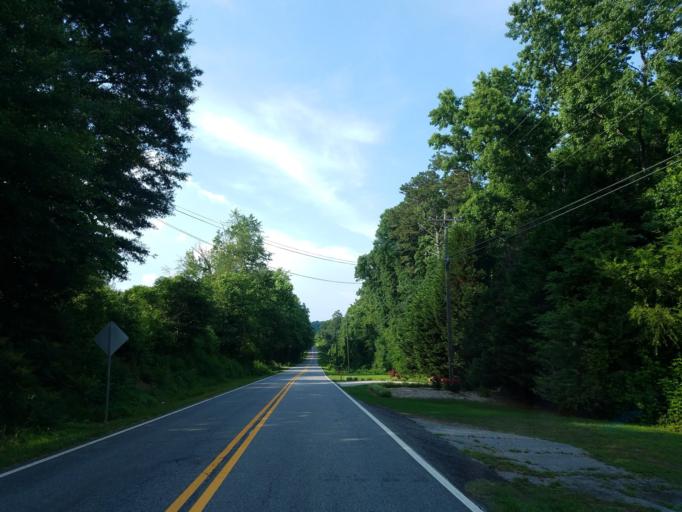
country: US
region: Georgia
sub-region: Forsyth County
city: Cumming
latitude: 34.2960
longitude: -84.0680
